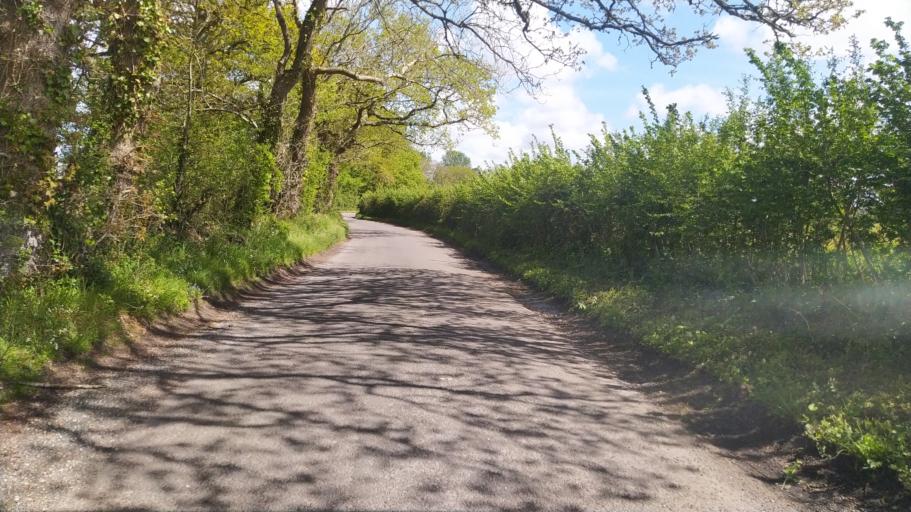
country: GB
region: England
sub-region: Hampshire
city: Fordingbridge
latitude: 50.8915
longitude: -1.7982
